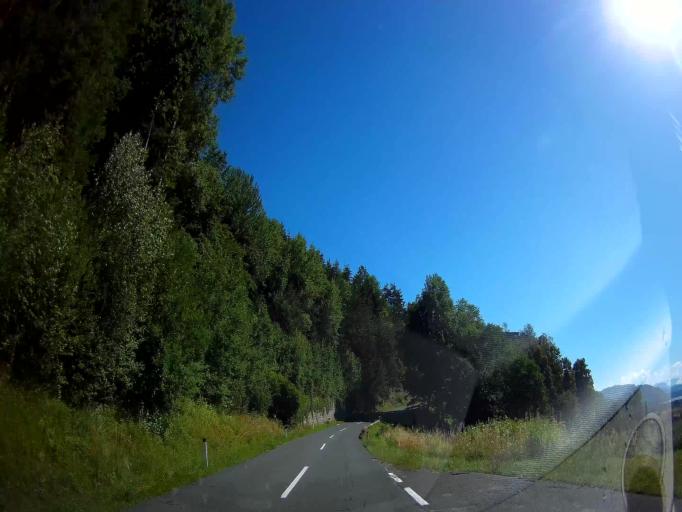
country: AT
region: Carinthia
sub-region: Politischer Bezirk Volkermarkt
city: Voelkermarkt
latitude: 46.6381
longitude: 14.5482
